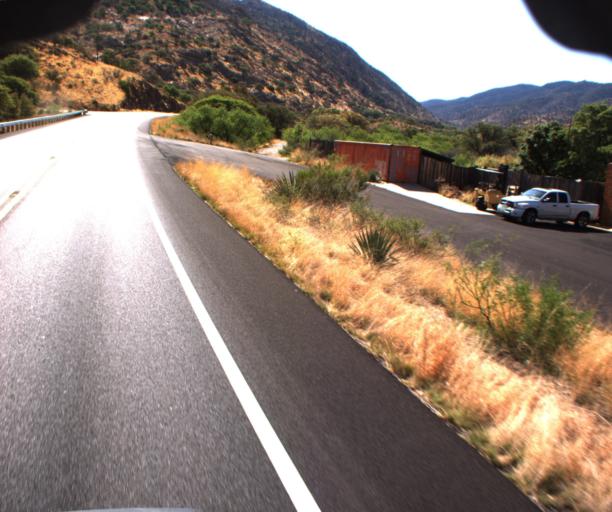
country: US
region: Arizona
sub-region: Cochise County
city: Bisbee
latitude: 31.4970
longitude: -109.9958
